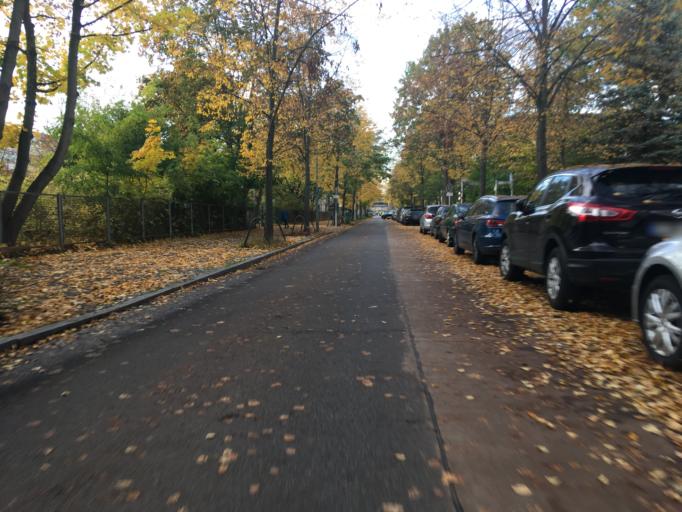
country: DE
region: Berlin
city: Niederschonhausen
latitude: 52.5825
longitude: 13.4189
